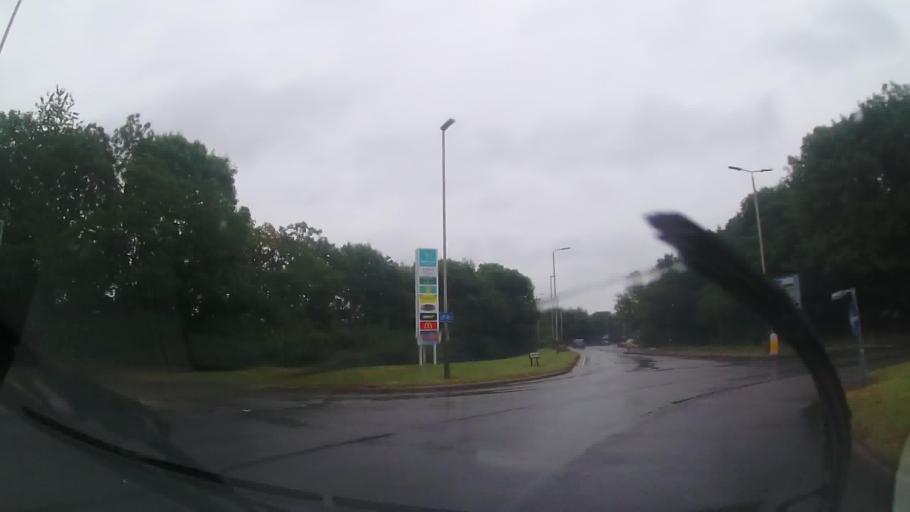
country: GB
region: England
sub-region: Leicestershire
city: Anstey
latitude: 52.6673
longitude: -1.1696
